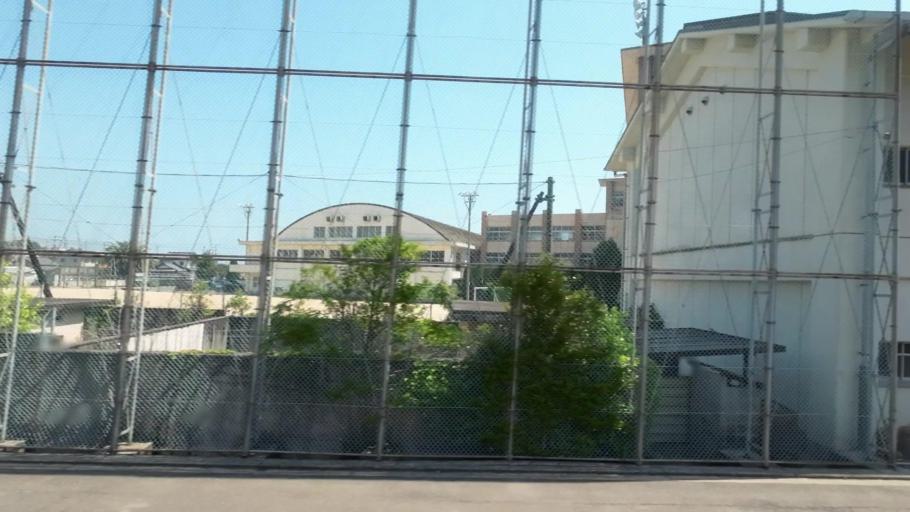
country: JP
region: Ehime
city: Saijo
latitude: 34.0165
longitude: 133.0328
